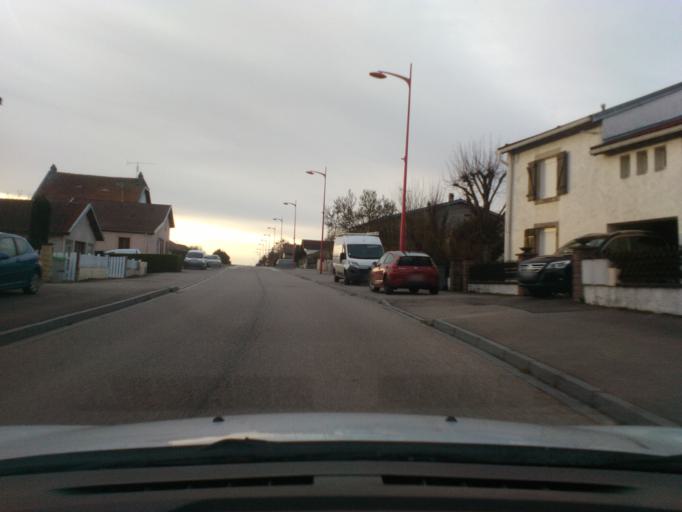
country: FR
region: Lorraine
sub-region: Departement des Vosges
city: Charmes
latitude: 48.3705
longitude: 6.3147
